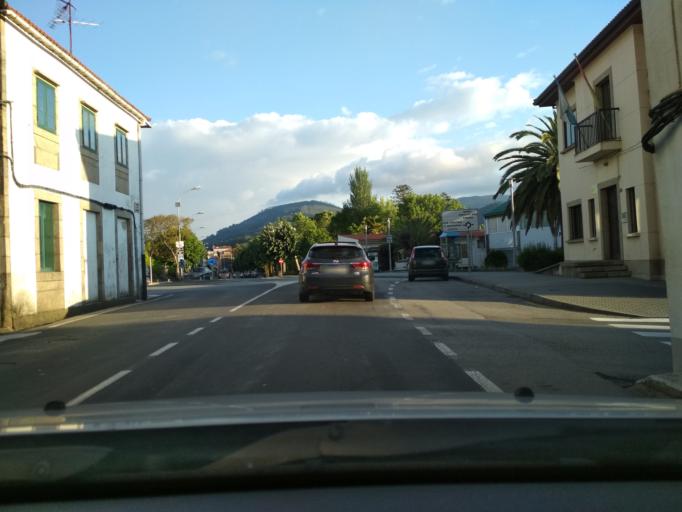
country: ES
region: Galicia
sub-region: Provincia da Coruna
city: Noia
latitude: 42.7871
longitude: -8.8886
